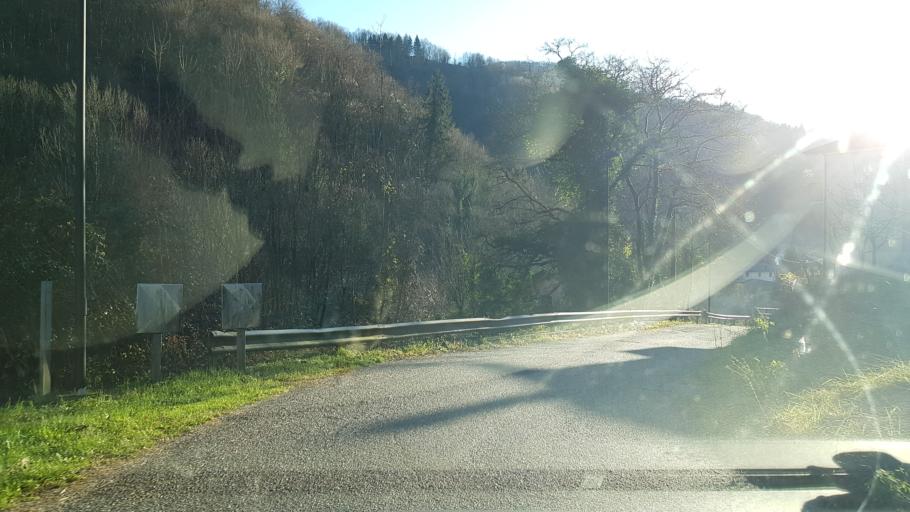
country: IT
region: Friuli Venezia Giulia
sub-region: Provincia di Udine
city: Savogna
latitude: 46.1605
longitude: 13.5351
